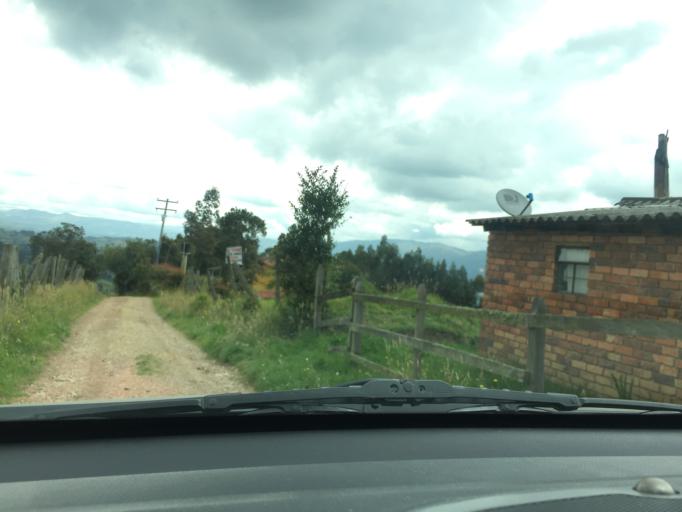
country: CO
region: Cundinamarca
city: Zipaquira
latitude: 5.0545
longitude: -74.0130
